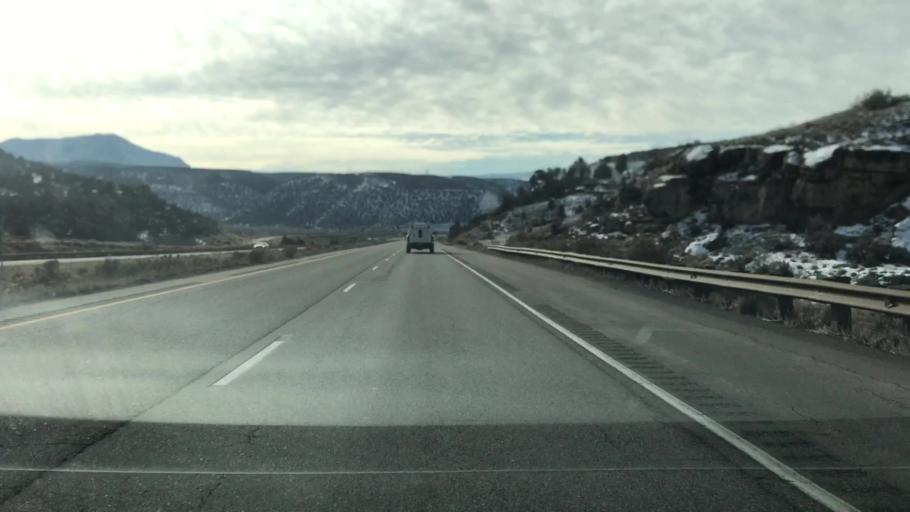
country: US
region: Colorado
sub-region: Garfield County
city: Parachute
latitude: 39.3648
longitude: -108.1702
